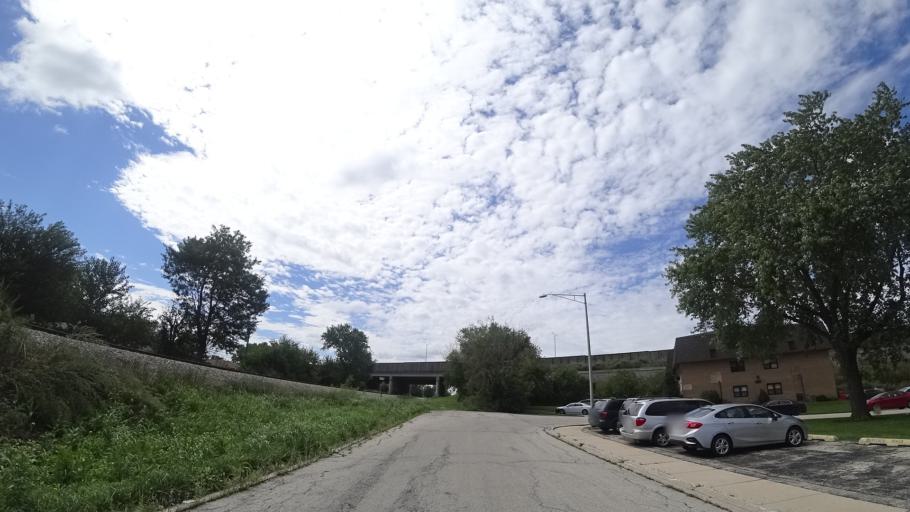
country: US
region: Illinois
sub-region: Cook County
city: Chicago Ridge
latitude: 41.7003
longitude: -87.7848
